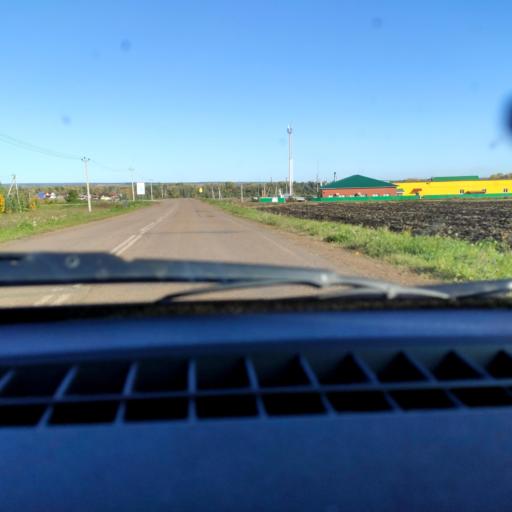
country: RU
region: Bashkortostan
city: Avdon
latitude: 54.5992
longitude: 55.7991
